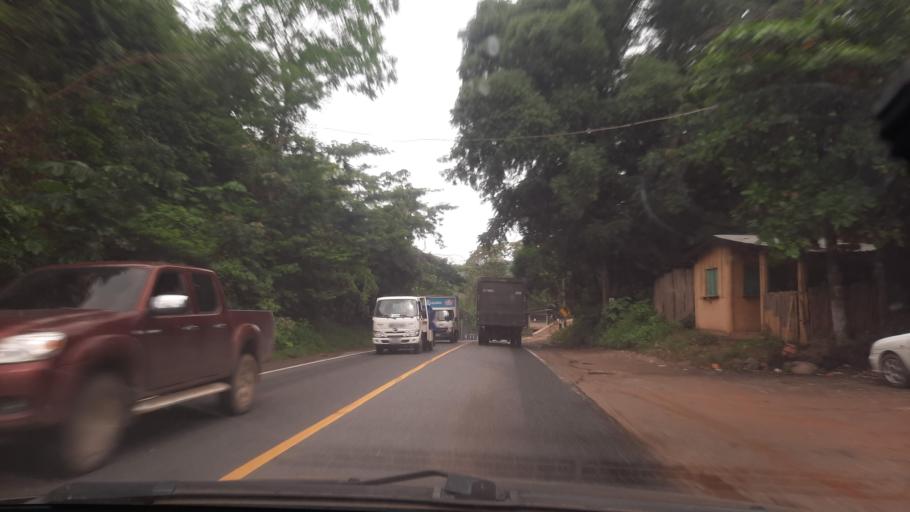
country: GT
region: Izabal
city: Morales
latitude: 15.4622
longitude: -88.9284
